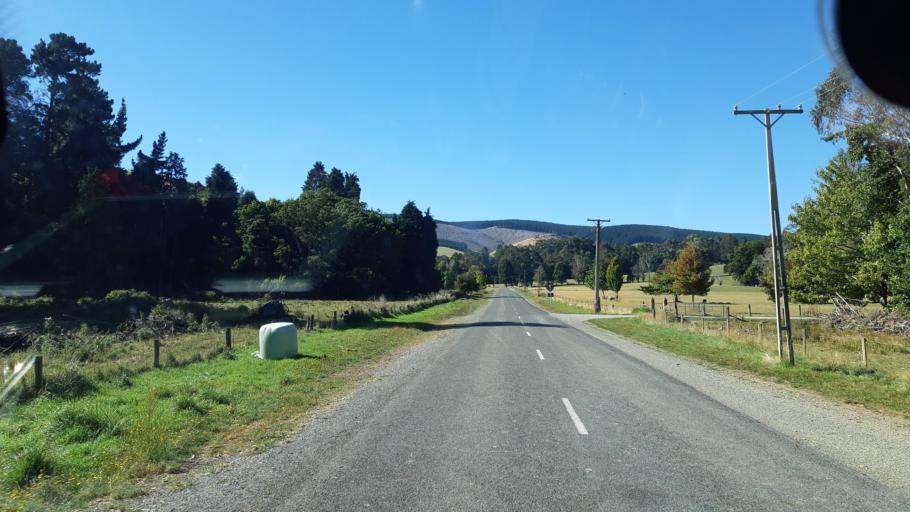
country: NZ
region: Southland
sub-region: Southland District
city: Winton
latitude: -45.8974
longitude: 168.3846
